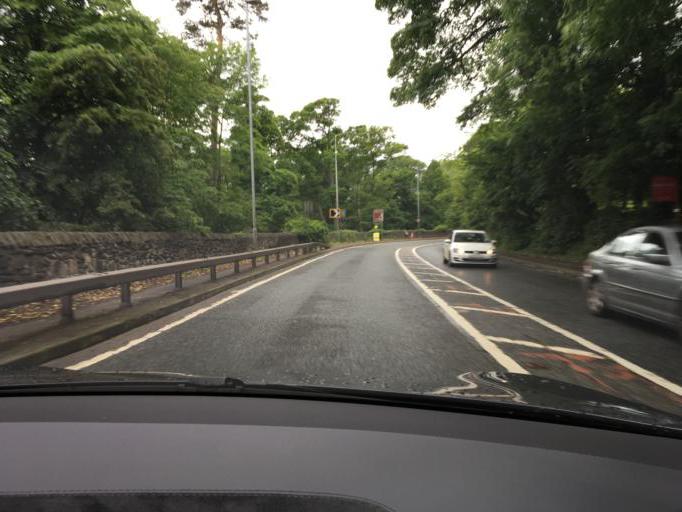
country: GB
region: England
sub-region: Cheshire East
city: Disley
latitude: 53.3559
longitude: -2.0517
